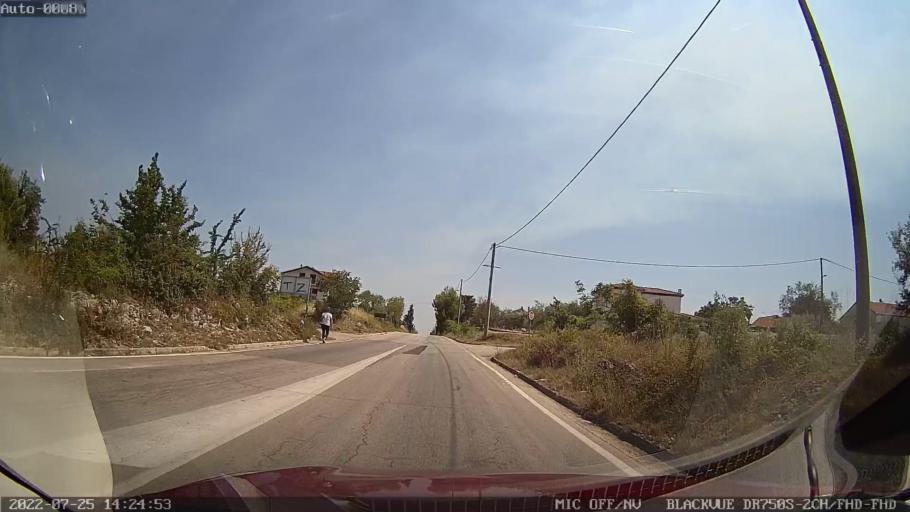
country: HR
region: Zadarska
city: Policnik
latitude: 44.1480
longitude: 15.3266
